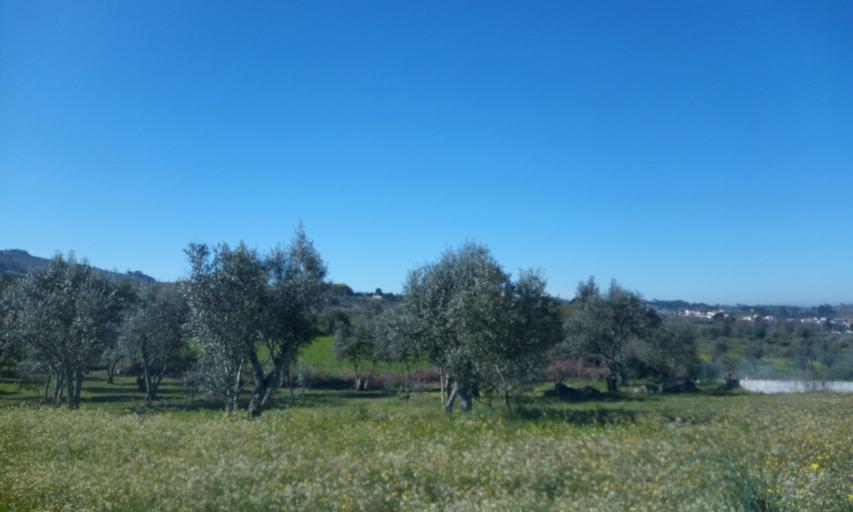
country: PT
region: Guarda
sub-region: Fornos de Algodres
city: Fornos de Algodres
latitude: 40.5256
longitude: -7.5578
